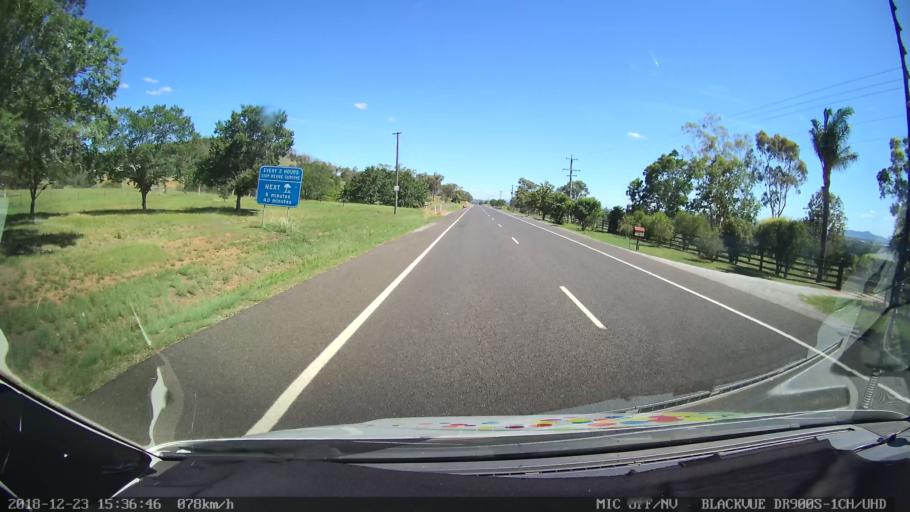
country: AU
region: New South Wales
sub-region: Tamworth Municipality
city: Tamworth
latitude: -31.0448
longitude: 150.8878
